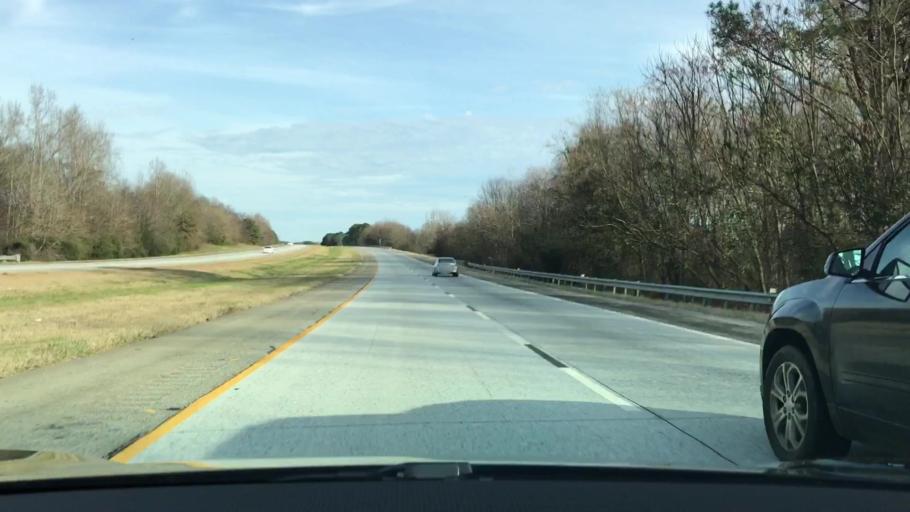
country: US
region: Georgia
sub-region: Morgan County
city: Madison
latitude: 33.5536
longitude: -83.4078
